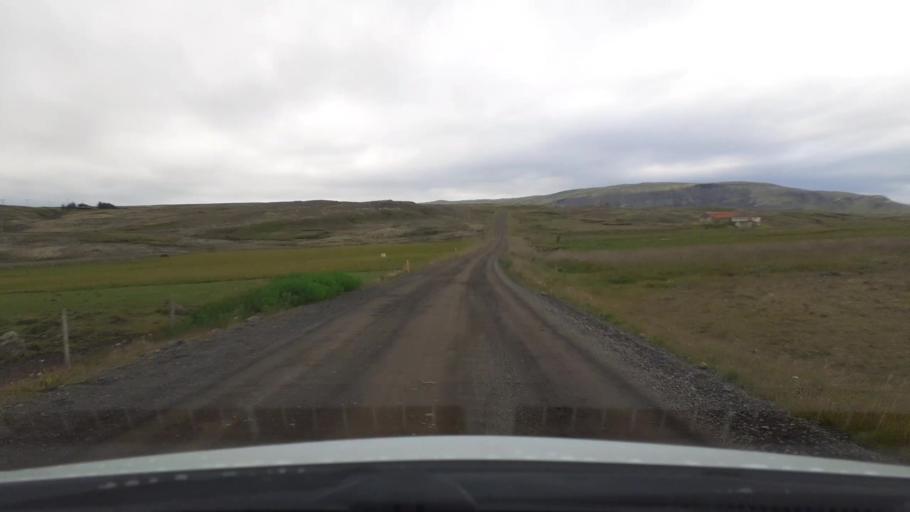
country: IS
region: Capital Region
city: Mosfellsbaer
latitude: 64.2036
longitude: -21.5609
